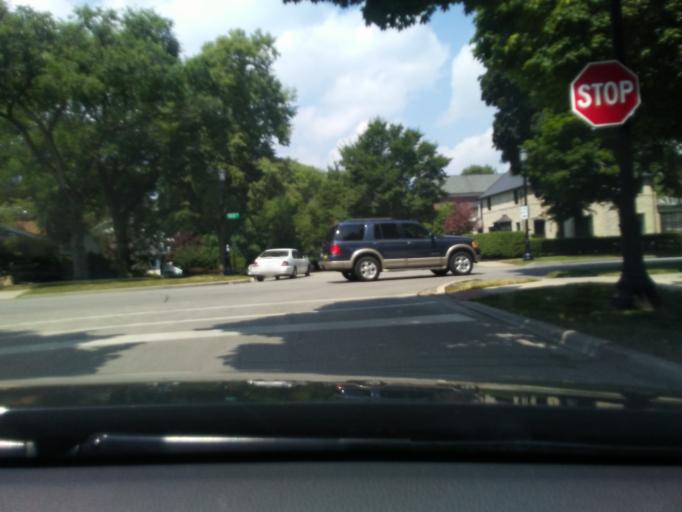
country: US
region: Illinois
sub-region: Cook County
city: Evanston
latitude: 42.0299
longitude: -87.6856
